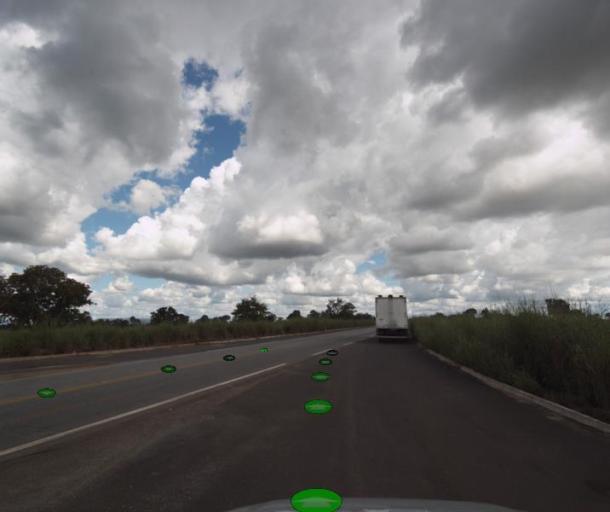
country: BR
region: Goias
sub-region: Porangatu
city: Porangatu
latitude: -13.4841
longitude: -49.1365
